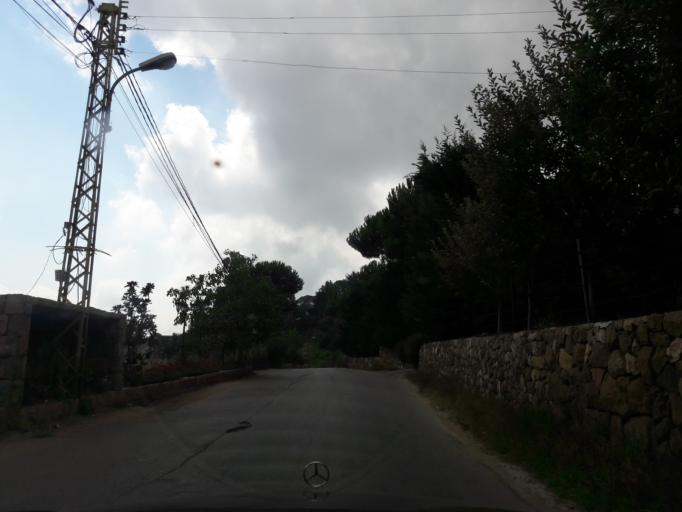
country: LB
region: Beqaa
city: Zahle
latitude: 33.9438
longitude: 35.7968
